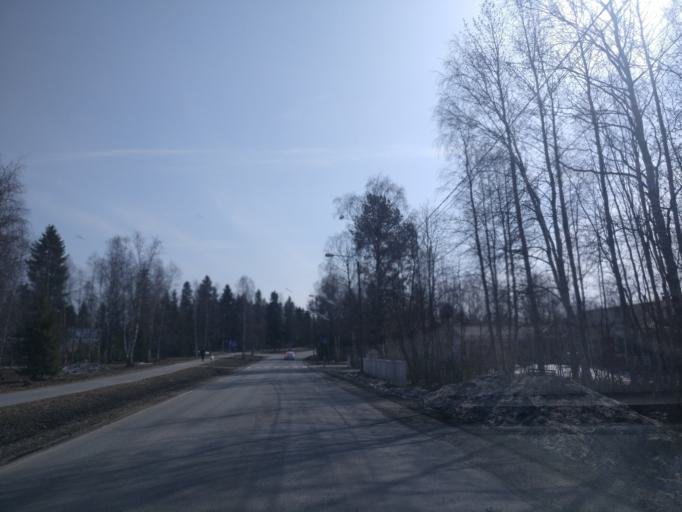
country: FI
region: Lapland
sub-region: Kemi-Tornio
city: Kemi
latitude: 65.7263
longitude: 24.6182
